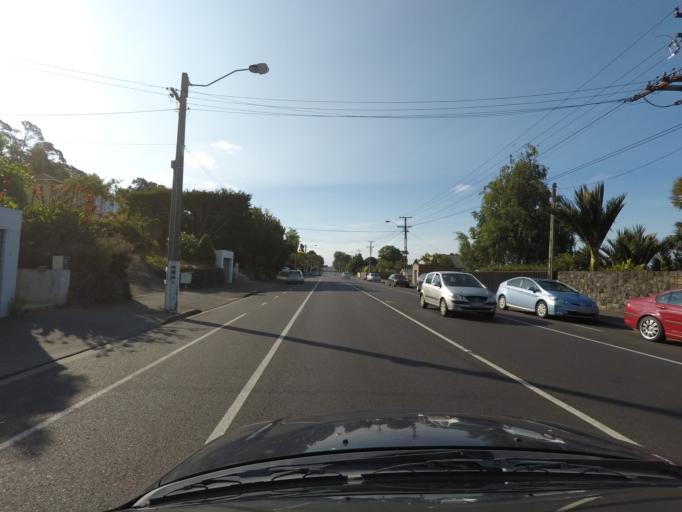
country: NZ
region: Auckland
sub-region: Auckland
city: Auckland
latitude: -36.8894
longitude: 174.7234
